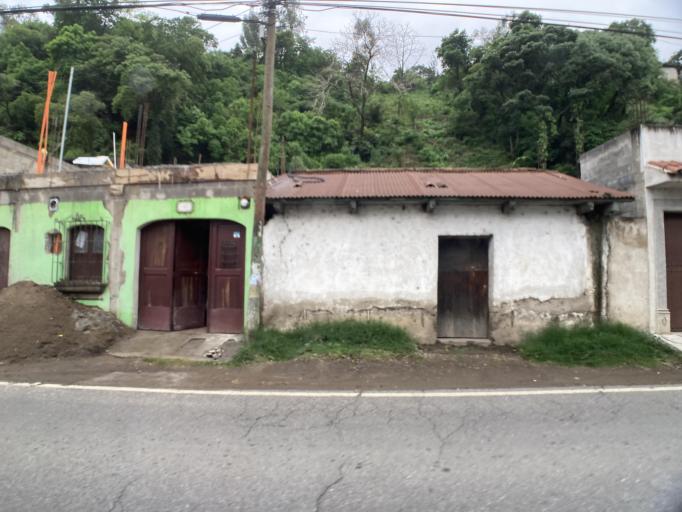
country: GT
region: Sacatepequez
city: Pastores
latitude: 14.6022
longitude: -90.7622
